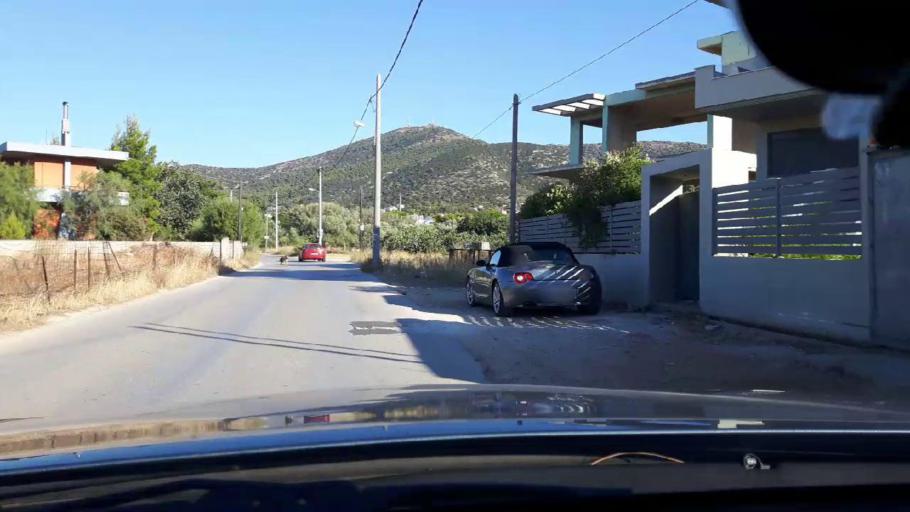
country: GR
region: Attica
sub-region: Nomarchia Anatolikis Attikis
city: Limin Mesoyaias
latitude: 37.8654
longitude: 24.0306
